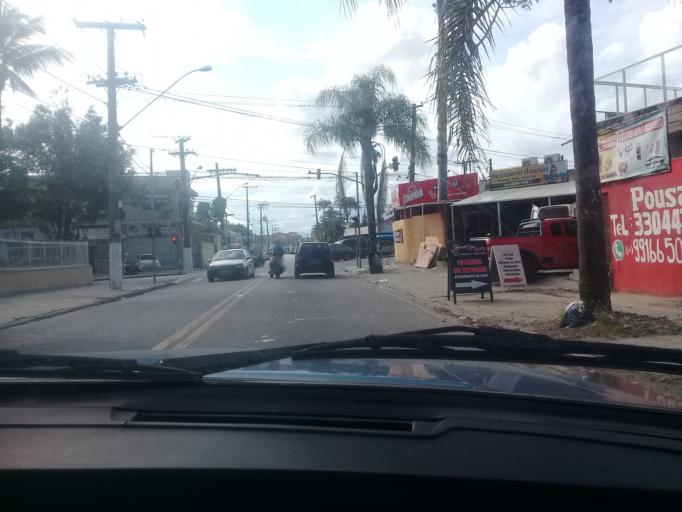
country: BR
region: Sao Paulo
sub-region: Guaruja
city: Guaruja
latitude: -24.0044
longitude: -46.2732
